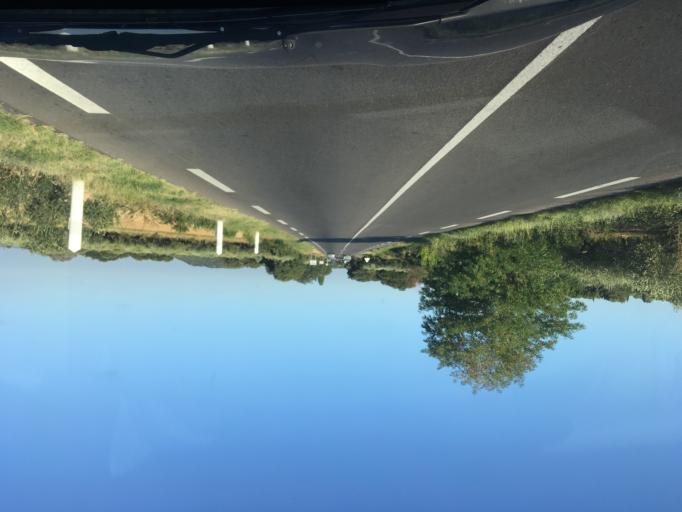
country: FR
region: Languedoc-Roussillon
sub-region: Departement du Gard
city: Bezouce
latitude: 43.8905
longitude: 4.5070
